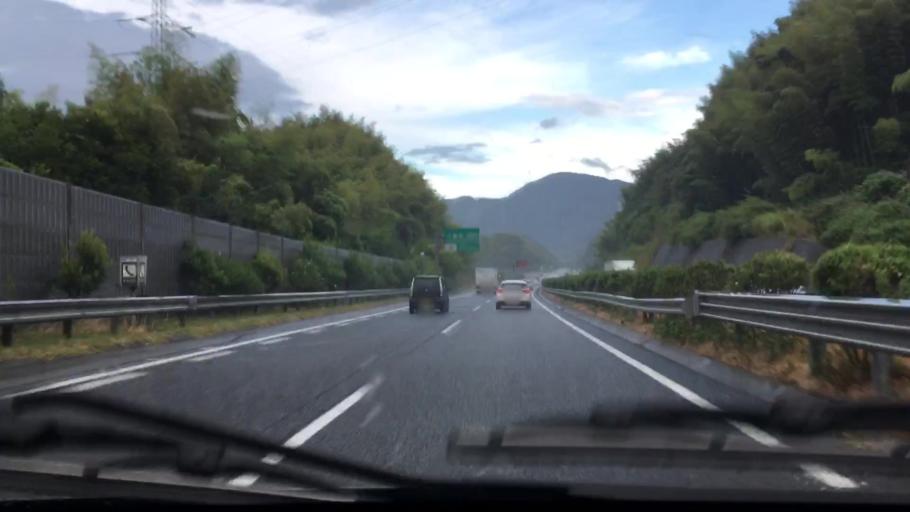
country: JP
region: Fukuoka
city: Kitakyushu
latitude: 33.8071
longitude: 130.8446
